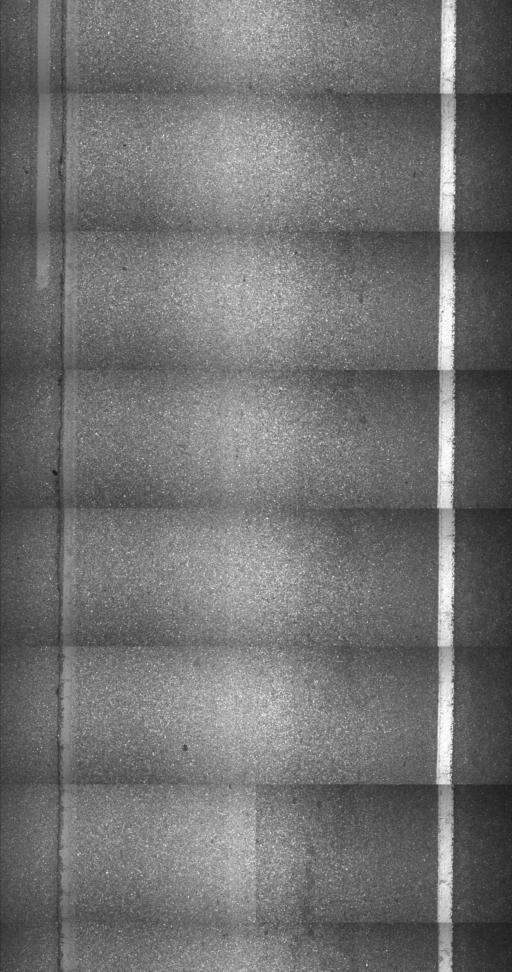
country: US
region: Vermont
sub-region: Addison County
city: Middlebury (village)
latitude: 43.8992
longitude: -73.2047
